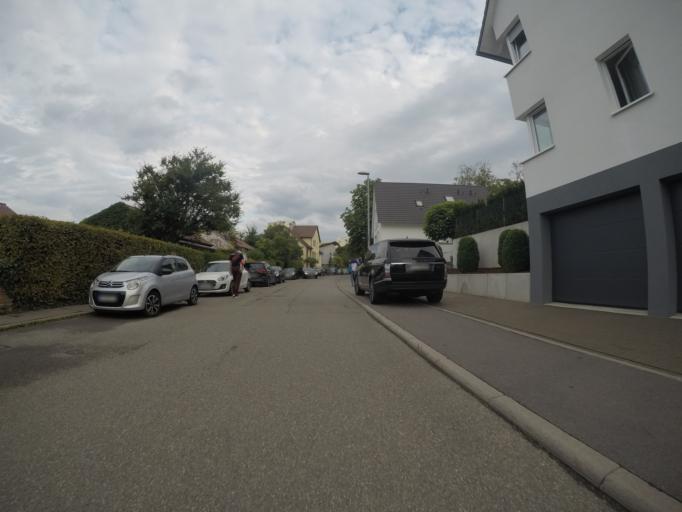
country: DE
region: Baden-Wuerttemberg
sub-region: Regierungsbezirk Stuttgart
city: Ostfildern
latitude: 48.7179
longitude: 9.2144
